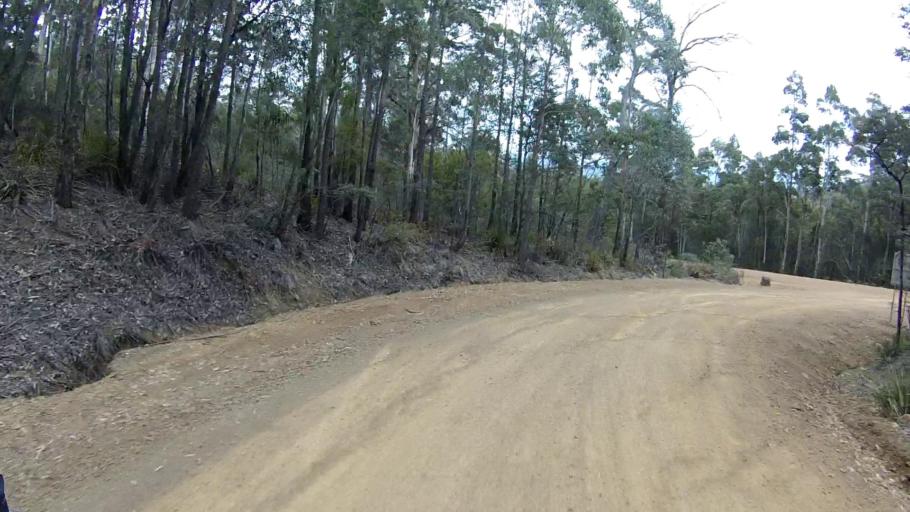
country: AU
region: Tasmania
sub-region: Sorell
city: Sorell
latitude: -42.6006
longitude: 147.8862
